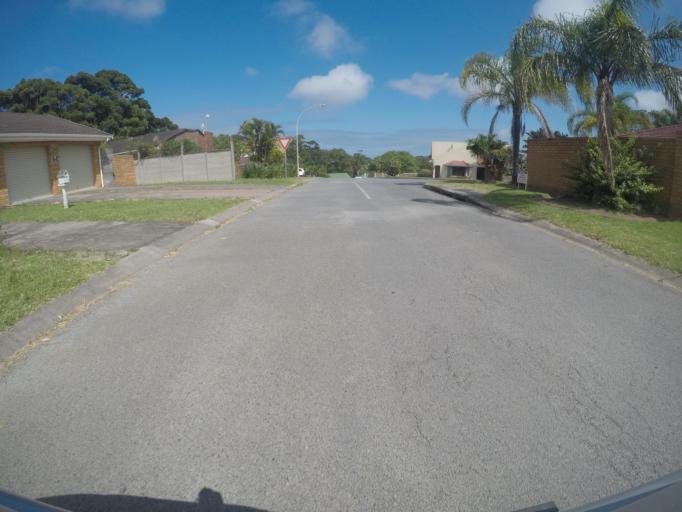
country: ZA
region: Eastern Cape
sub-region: Buffalo City Metropolitan Municipality
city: East London
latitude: -32.9977
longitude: 27.8884
